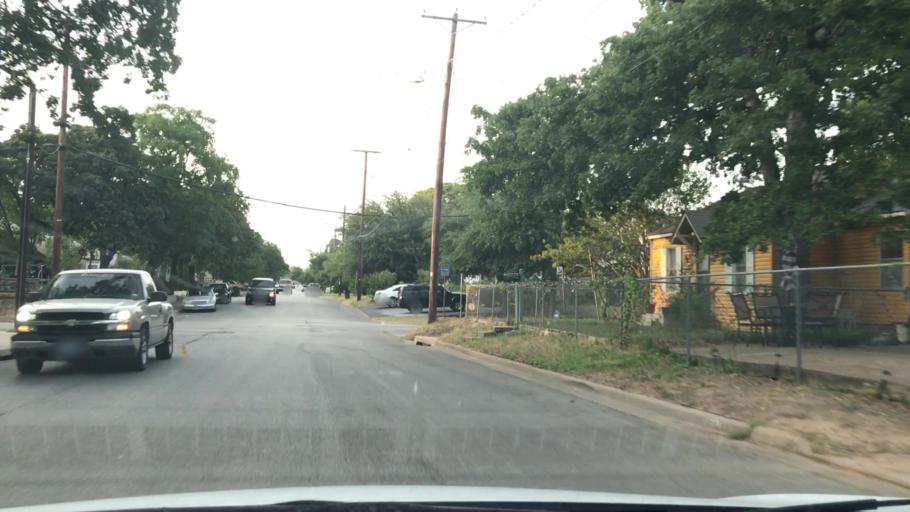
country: US
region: Texas
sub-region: Tarrant County
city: Haltom City
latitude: 32.7910
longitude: -97.2823
